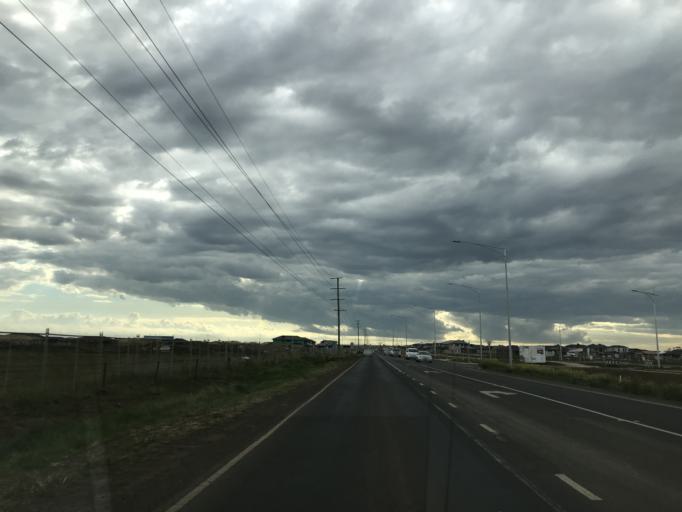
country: AU
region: Victoria
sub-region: Wyndham
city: Truganina
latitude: -37.8224
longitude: 144.7184
